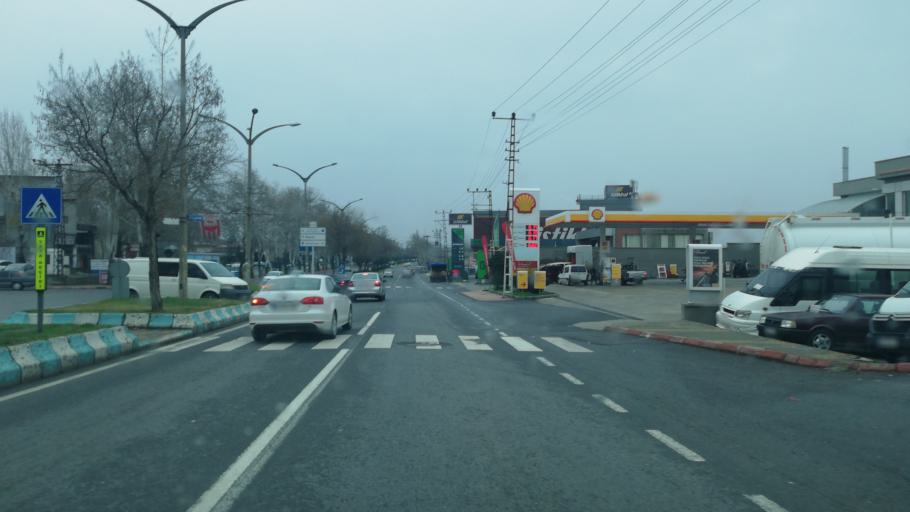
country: TR
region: Kahramanmaras
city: Kahramanmaras
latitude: 37.5648
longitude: 36.9512
